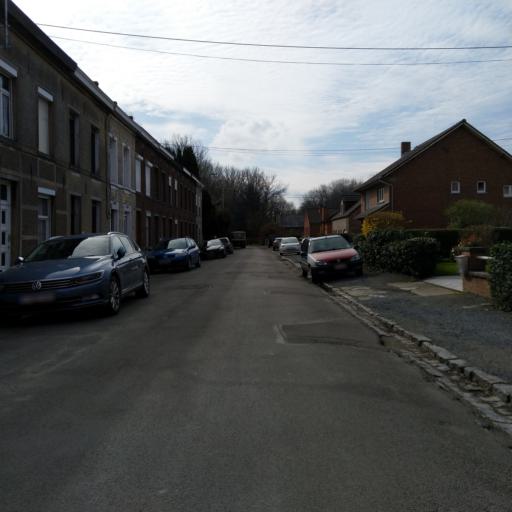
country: BE
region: Wallonia
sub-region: Province du Hainaut
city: Soignies
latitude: 50.5730
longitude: 4.0593
